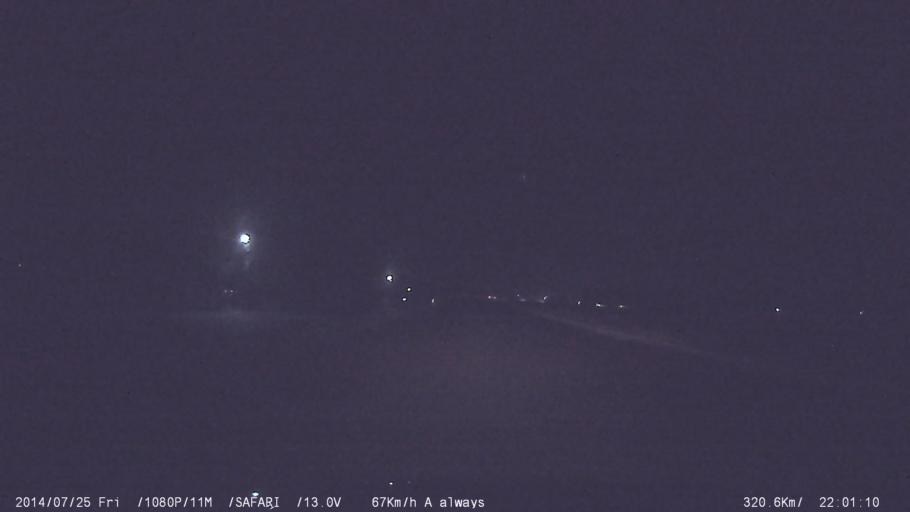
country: IN
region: Tamil Nadu
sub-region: Tiruppur
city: Avinashi
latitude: 11.1620
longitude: 77.2252
